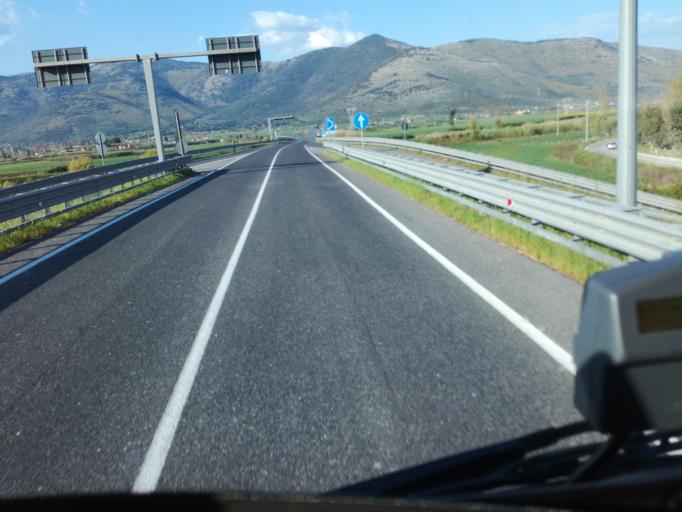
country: IT
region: Latium
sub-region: Provincia di Latina
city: Roccasecca dei Volsci
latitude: 41.4838
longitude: 13.2041
